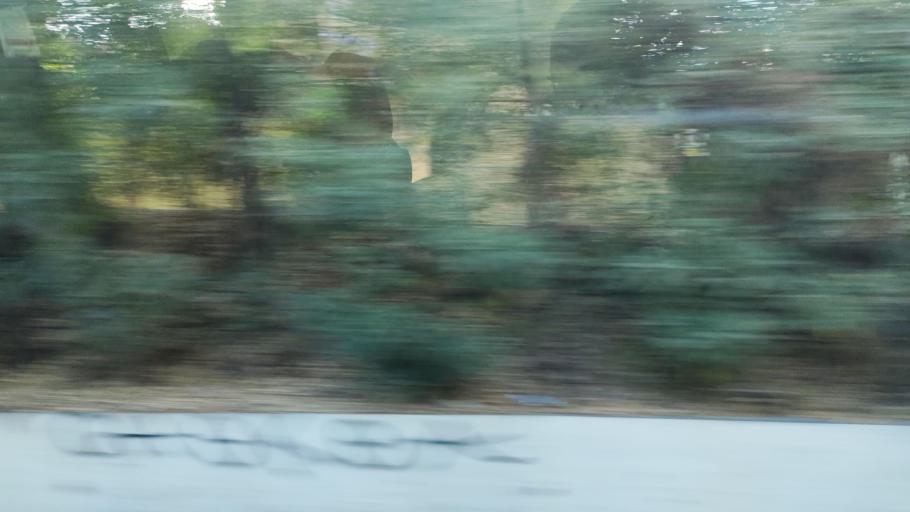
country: ES
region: Andalusia
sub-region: Provincia de Malaga
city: Torremolinos
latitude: 36.6361
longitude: -4.4992
